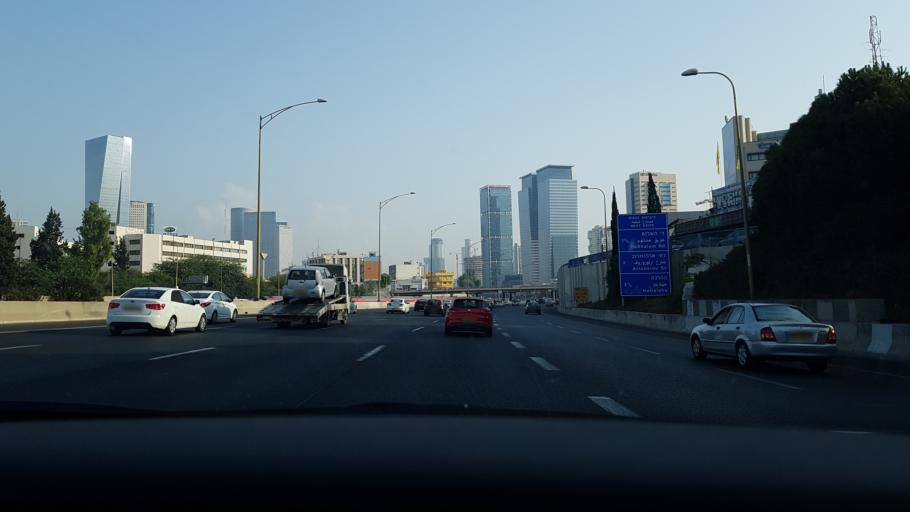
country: IL
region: Tel Aviv
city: Tel Aviv
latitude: 32.0621
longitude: 34.7877
